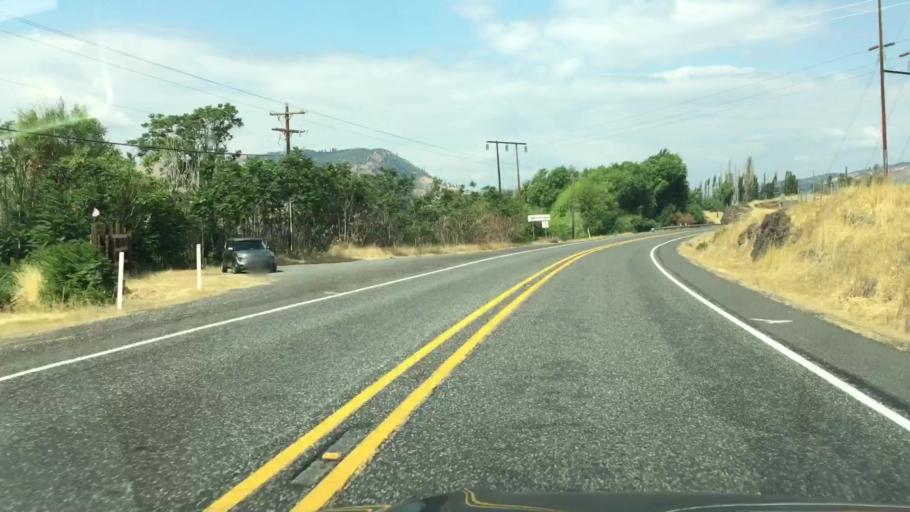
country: US
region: Washington
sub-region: Klickitat County
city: Dallesport
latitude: 45.6492
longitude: -121.1828
